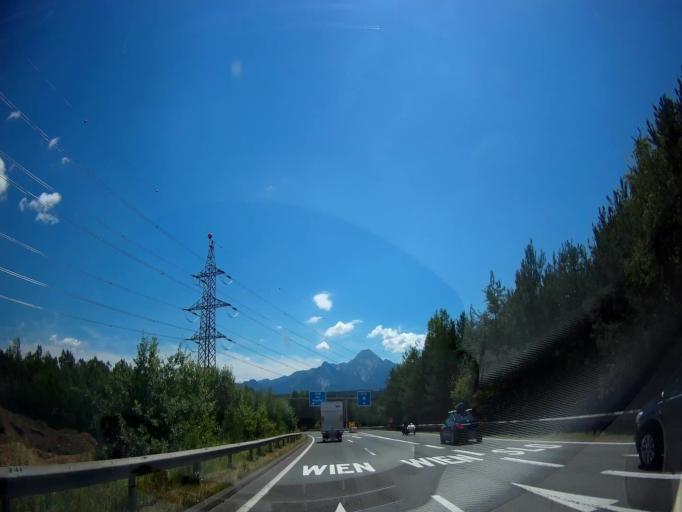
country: AT
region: Carinthia
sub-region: Politischer Bezirk Villach Land
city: Wernberg
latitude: 46.6209
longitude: 13.8997
